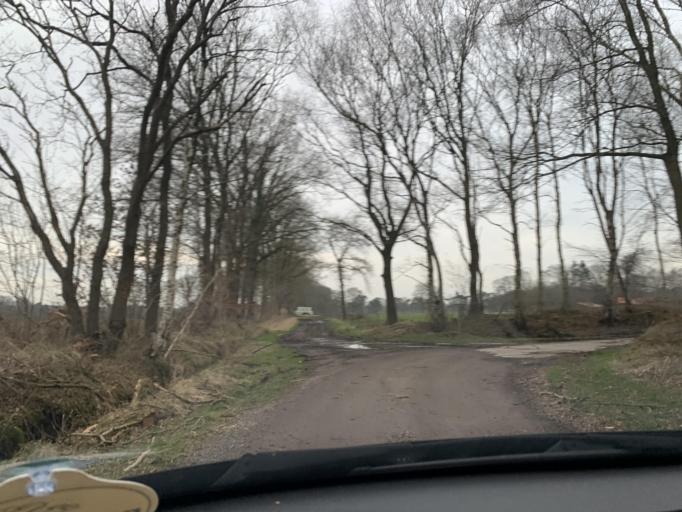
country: DE
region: Lower Saxony
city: Bad Zwischenahn
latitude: 53.2139
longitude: 7.9833
